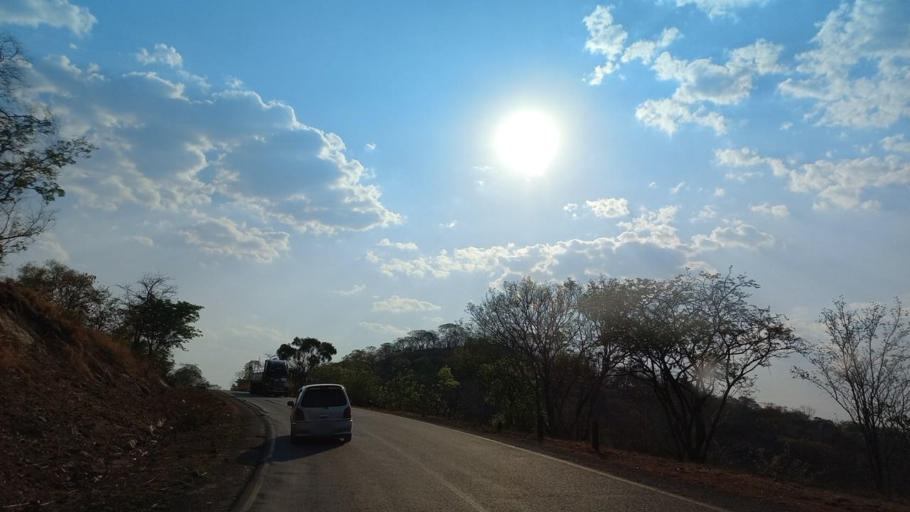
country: ZM
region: Lusaka
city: Luangwa
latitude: -14.9728
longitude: 30.0080
